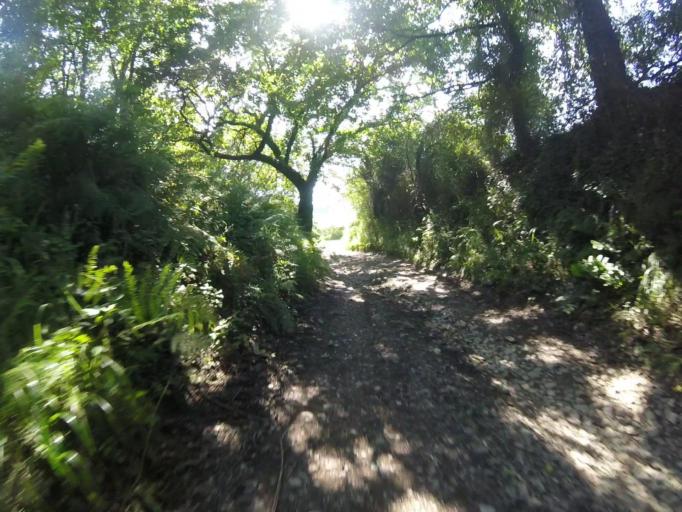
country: ES
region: Basque Country
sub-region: Provincia de Guipuzcoa
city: Astigarraga
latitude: 43.2581
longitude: -1.9369
